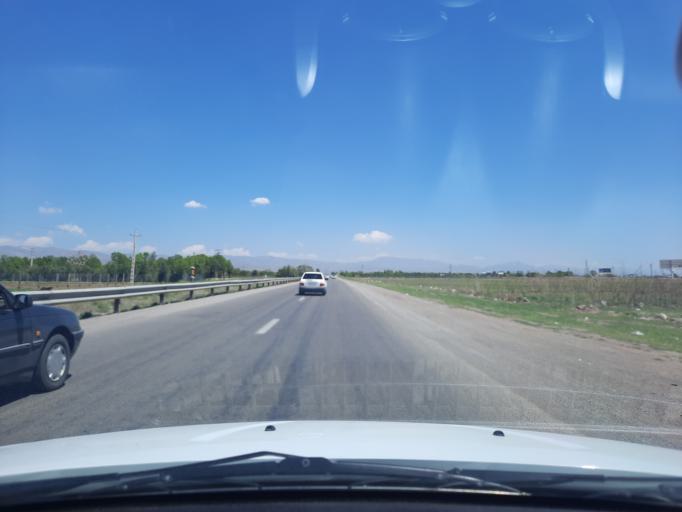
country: IR
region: Qazvin
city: Qazvin
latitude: 36.2645
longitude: 50.0639
